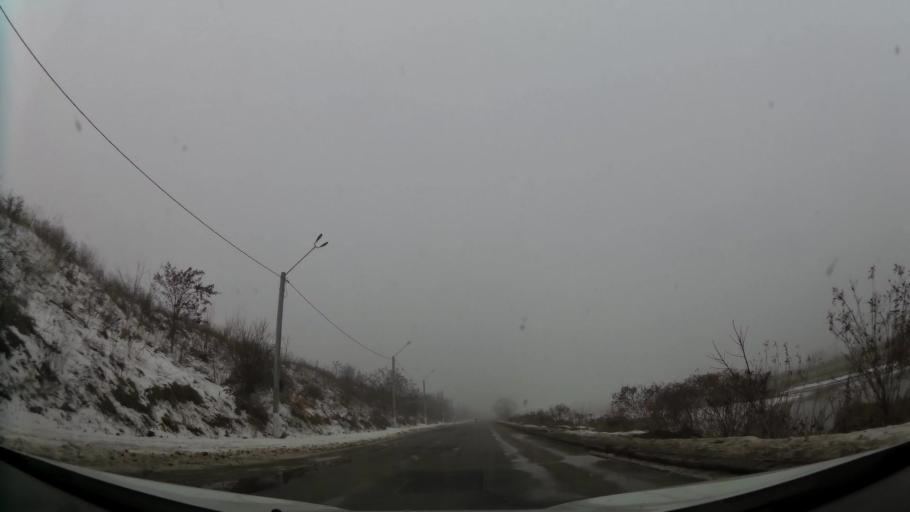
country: RO
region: Ilfov
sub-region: Comuna Chiajna
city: Chiajna
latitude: 44.4634
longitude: 25.9909
